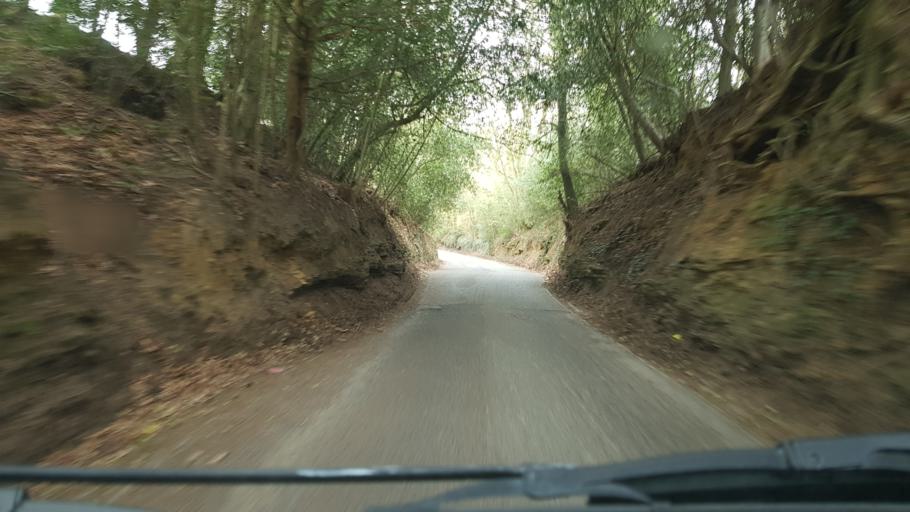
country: GB
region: England
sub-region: Surrey
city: Cranleigh
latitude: 51.1886
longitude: -0.4641
